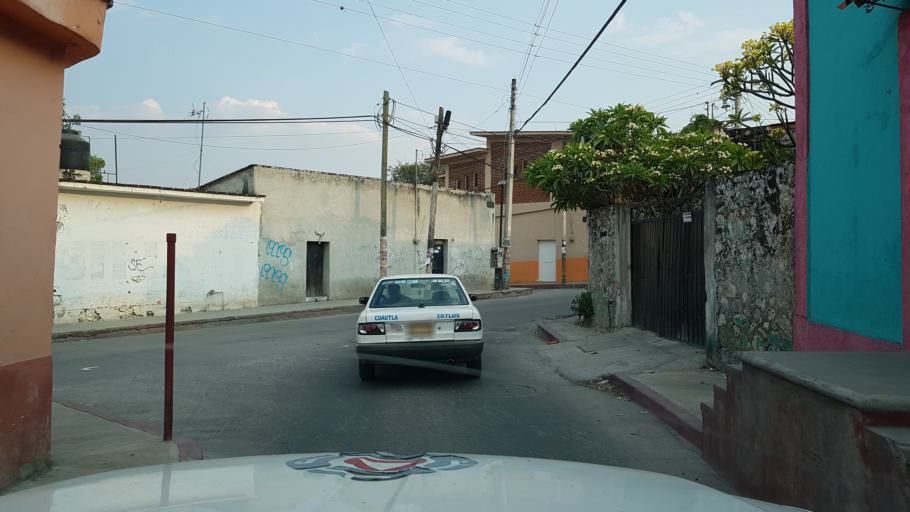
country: MX
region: Morelos
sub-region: Ayala
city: Ciudad Ayala
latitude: 18.7675
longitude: -98.9840
